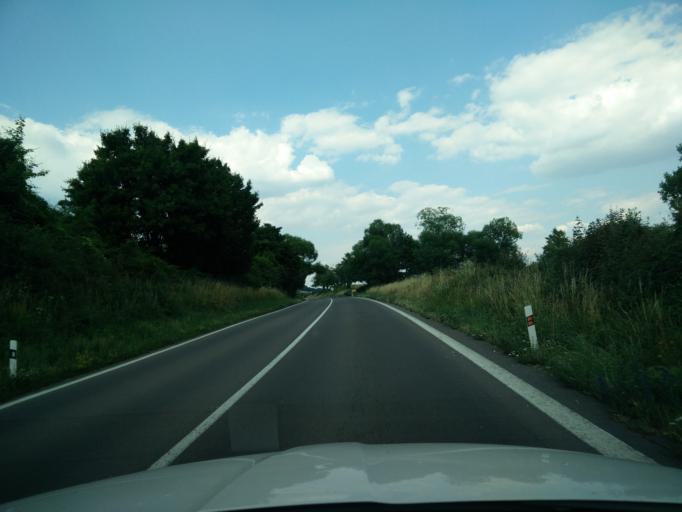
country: SK
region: Nitriansky
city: Novaky
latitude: 48.7170
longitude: 18.4607
